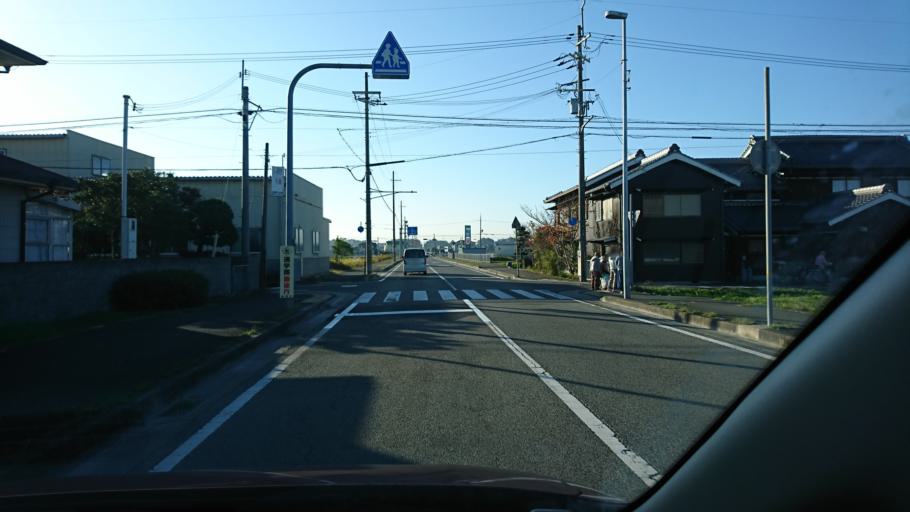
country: JP
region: Hyogo
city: Miki
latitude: 34.7627
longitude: 134.9197
